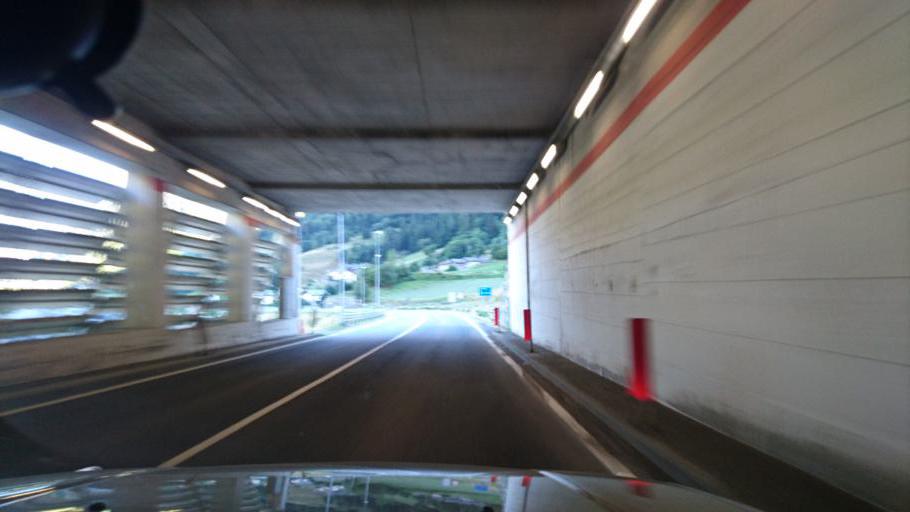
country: IT
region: Aosta Valley
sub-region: Valle d'Aosta
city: Etroubles
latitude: 45.8125
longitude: 7.2380
